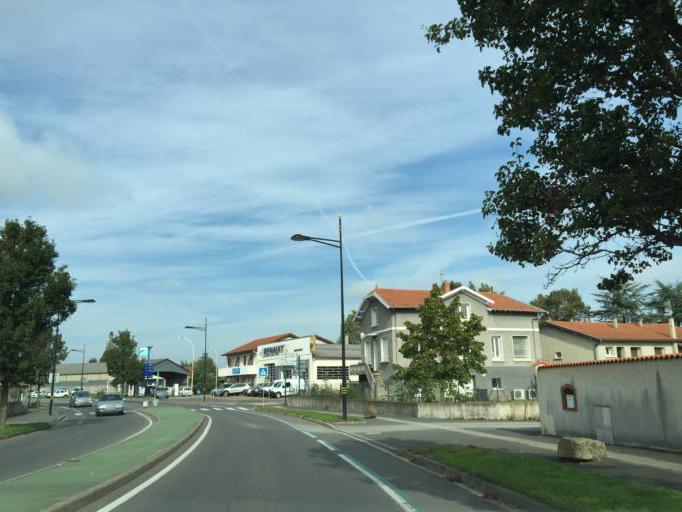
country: FR
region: Rhone-Alpes
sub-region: Departement de la Loire
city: Sury-le-Comtal
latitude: 45.5414
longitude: 4.1866
